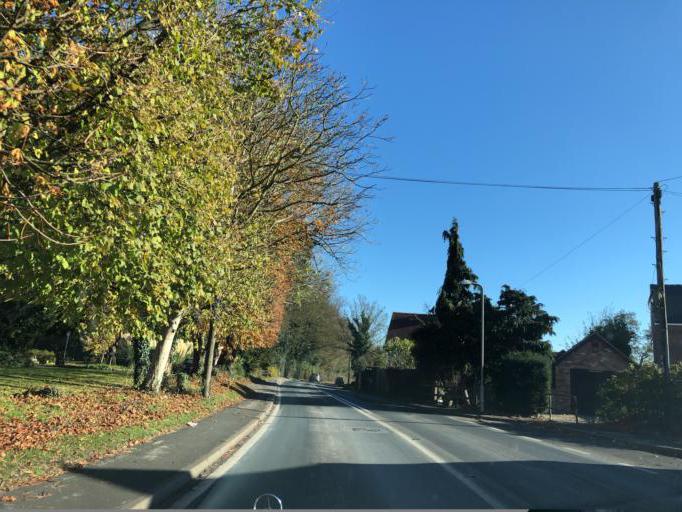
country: GB
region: England
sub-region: Warwickshire
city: Harbury
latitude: 52.2558
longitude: -1.4458
